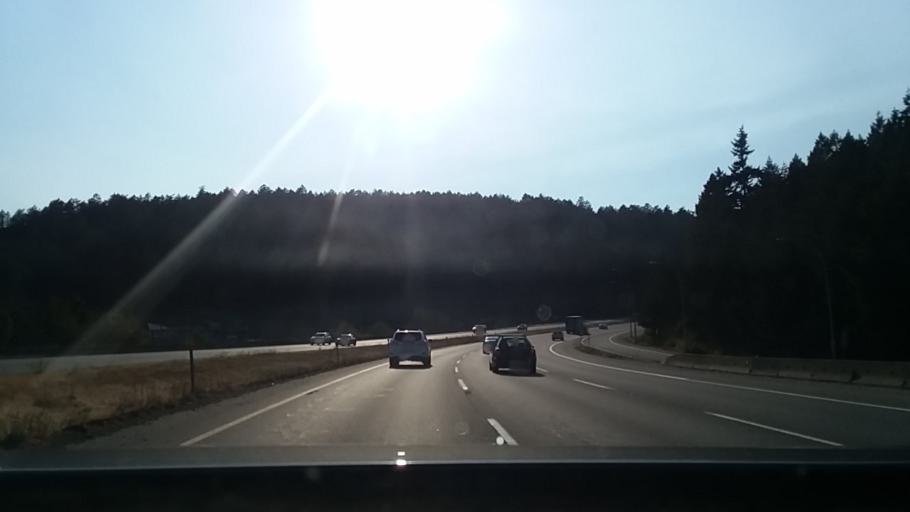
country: CA
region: British Columbia
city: Colwood
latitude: 48.4615
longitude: -123.4673
